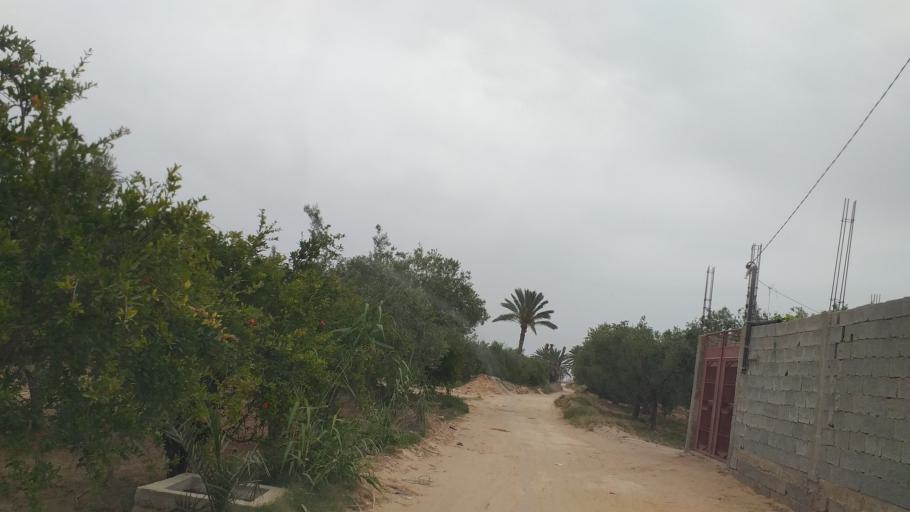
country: TN
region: Qabis
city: Gabes
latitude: 33.9550
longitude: 10.0600
